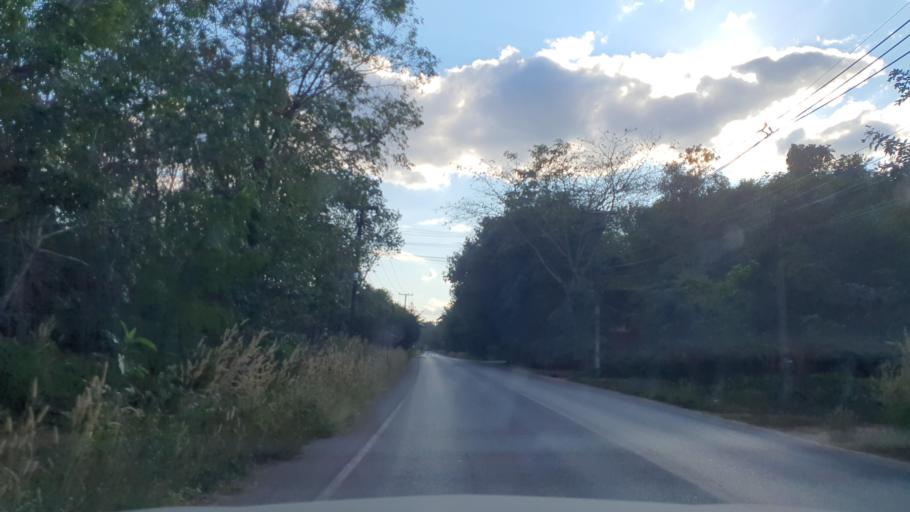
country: TH
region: Changwat Bueng Kan
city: Si Wilai
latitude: 18.1397
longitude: 103.8891
